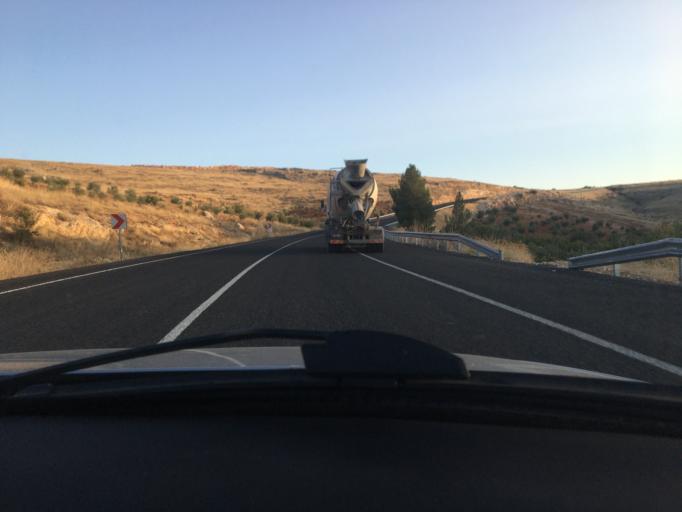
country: TR
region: Sanliurfa
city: Bogurtlen
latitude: 37.1858
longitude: 37.9753
